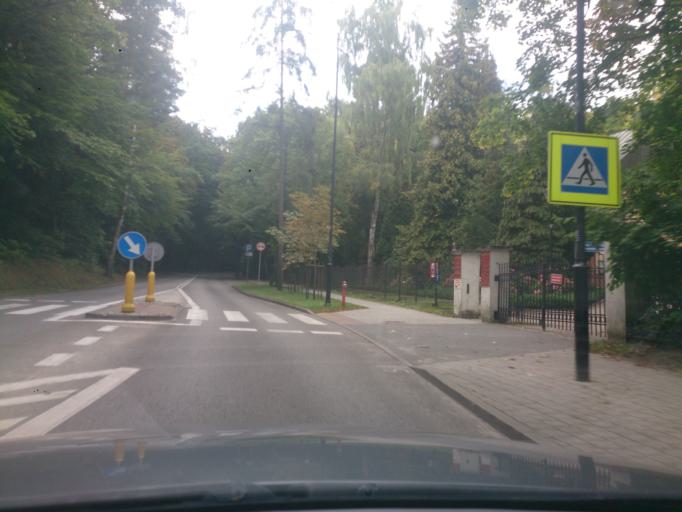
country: PL
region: Pomeranian Voivodeship
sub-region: Sopot
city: Sopot
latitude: 54.4511
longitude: 18.5460
